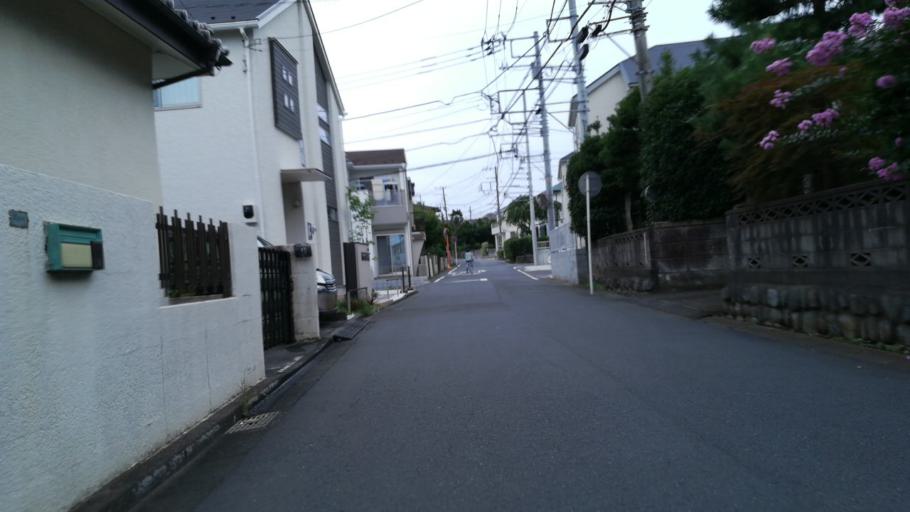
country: JP
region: Tokyo
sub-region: Machida-shi
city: Machida
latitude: 35.5704
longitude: 139.4085
